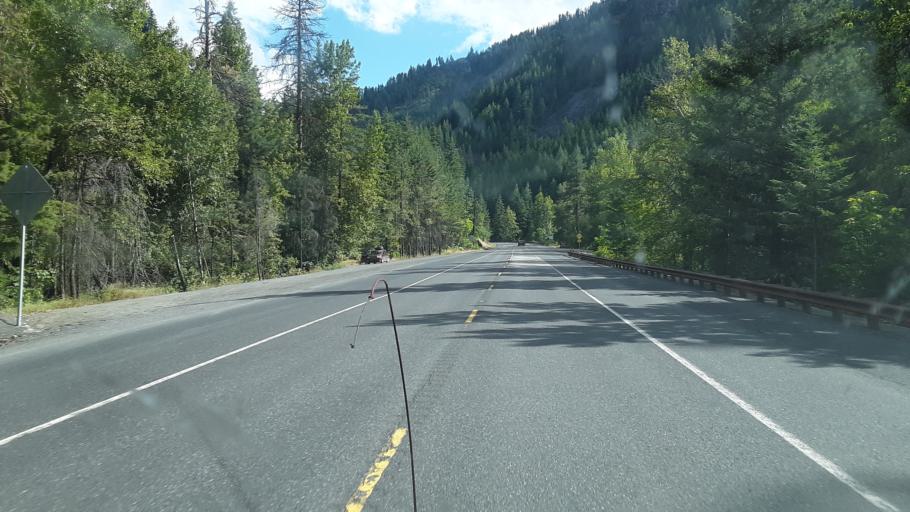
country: US
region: Washington
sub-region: Chelan County
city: Leavenworth
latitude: 47.4651
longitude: -120.6594
